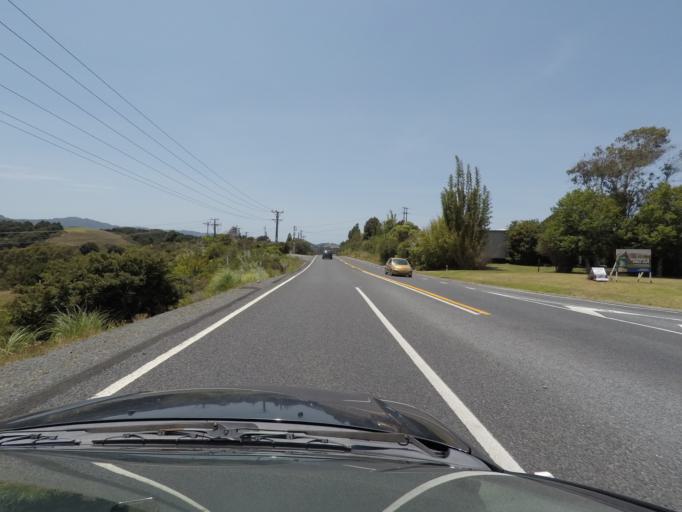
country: NZ
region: Auckland
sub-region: Auckland
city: Warkworth
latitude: -36.3765
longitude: 174.6717
